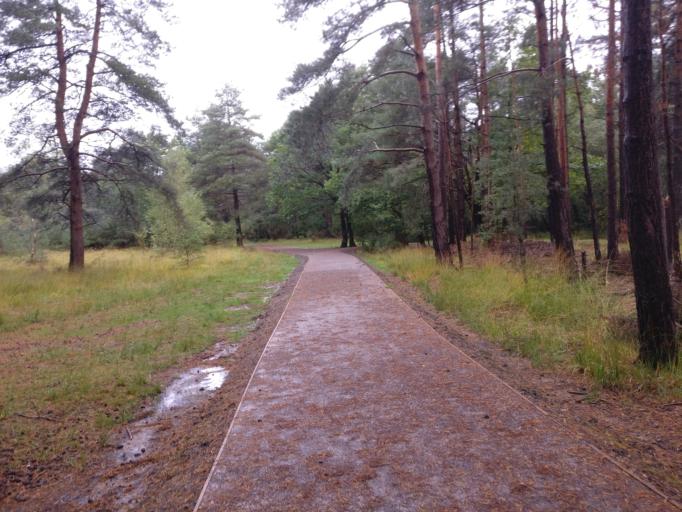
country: GB
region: England
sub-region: Surrey
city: Frimley
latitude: 51.3179
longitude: -0.7121
